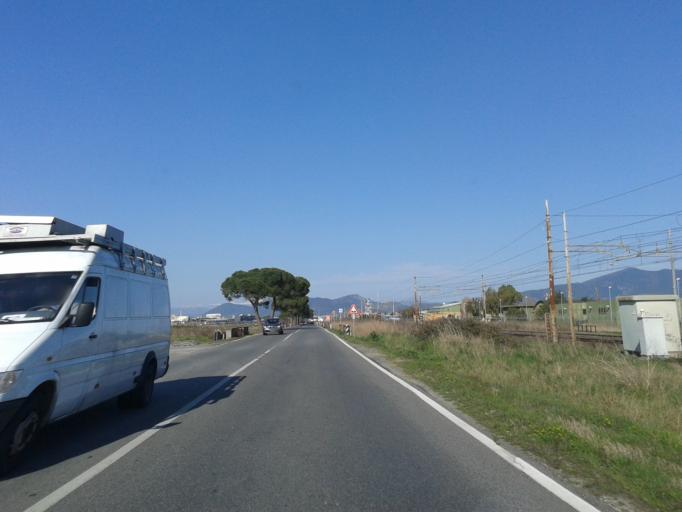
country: IT
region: Tuscany
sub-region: Province of Pisa
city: Pisa
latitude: 43.6853
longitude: 10.3824
